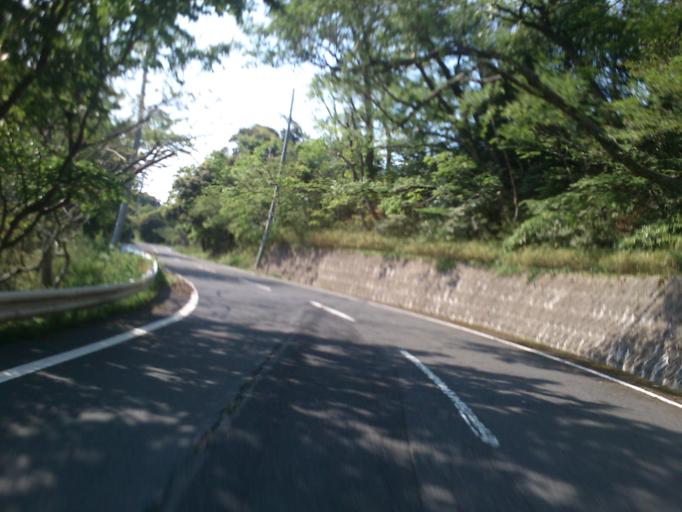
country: JP
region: Kyoto
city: Miyazu
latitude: 35.7461
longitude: 135.1726
